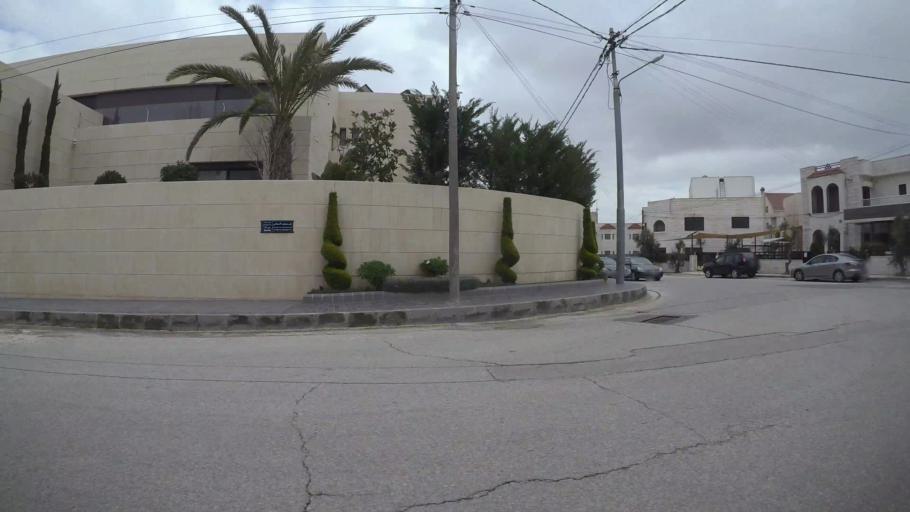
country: JO
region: Amman
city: Wadi as Sir
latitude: 31.9862
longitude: 35.8341
